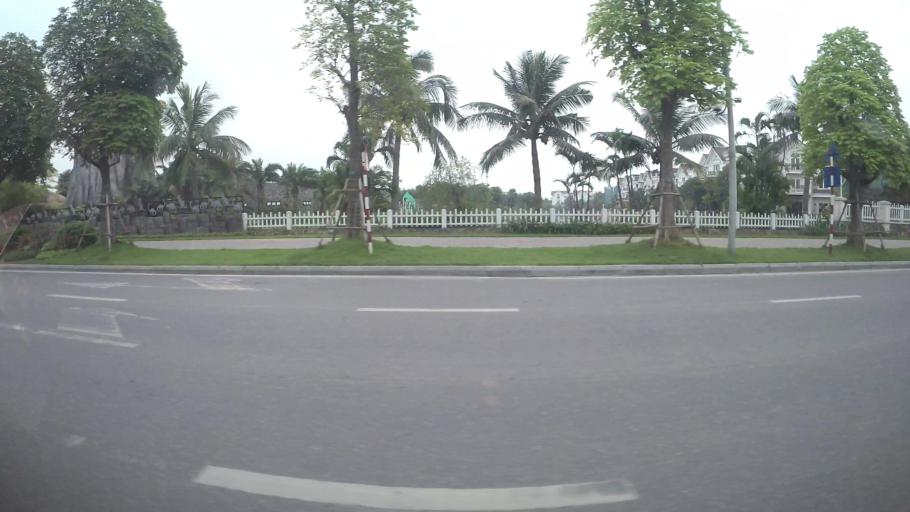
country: VN
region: Ha Noi
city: Trau Quy
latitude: 21.0494
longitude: 105.9158
